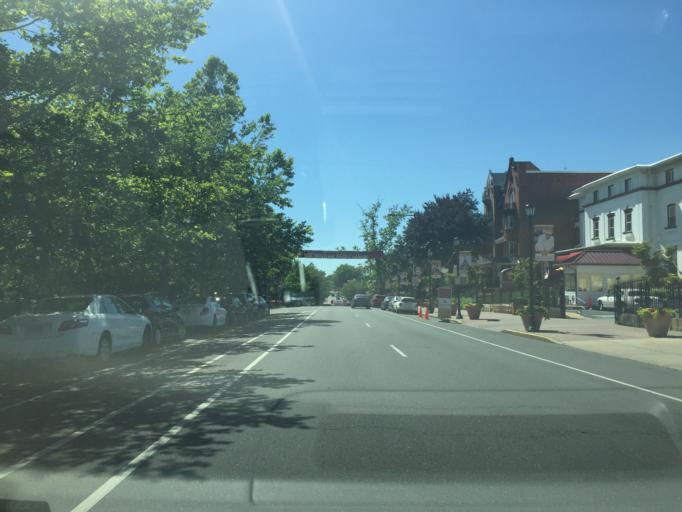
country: US
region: Pennsylvania
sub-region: Philadelphia County
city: Philadelphia
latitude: 39.9546
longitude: -75.2069
